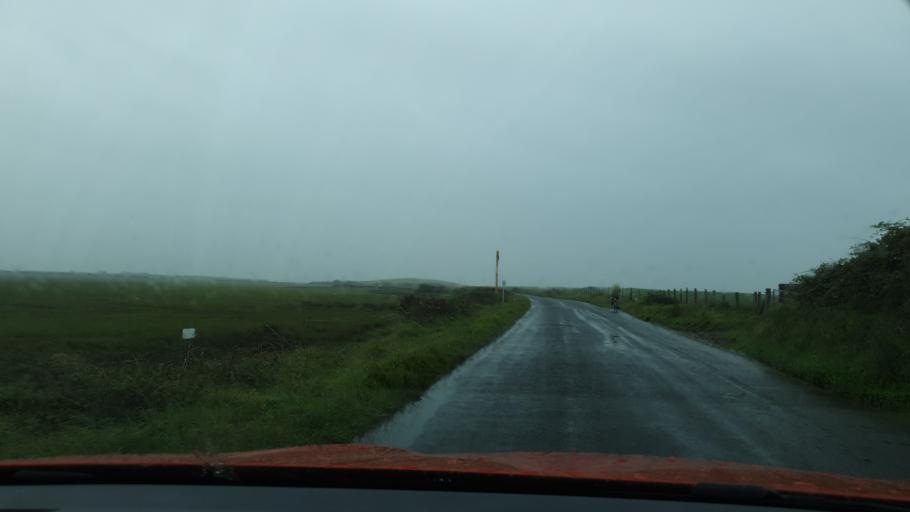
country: GB
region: England
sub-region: Cumbria
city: Barrow in Furness
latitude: 54.0719
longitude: -3.2276
